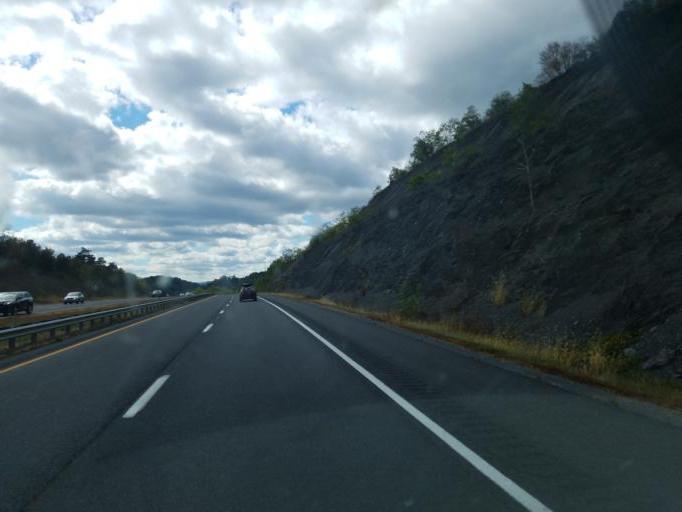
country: US
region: Maryland
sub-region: Allegany County
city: Cumberland
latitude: 39.6775
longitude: -78.6867
